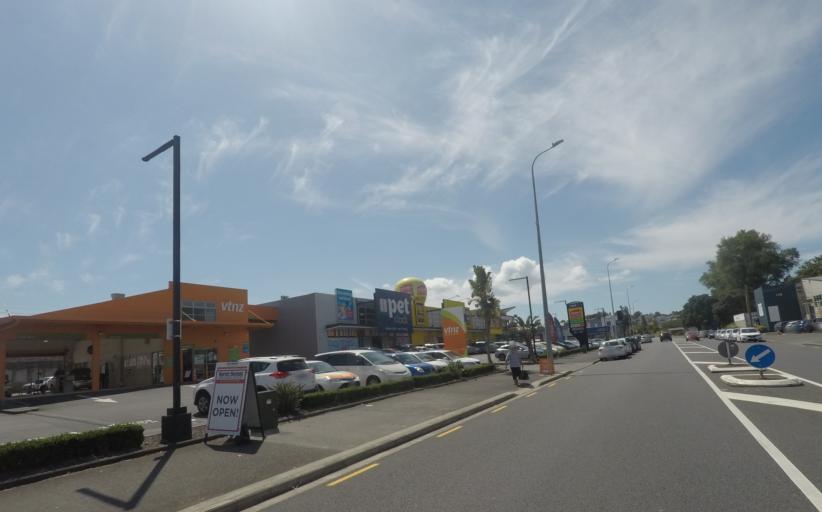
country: NZ
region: Auckland
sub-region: Auckland
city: Tamaki
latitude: -36.8749
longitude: 174.8539
